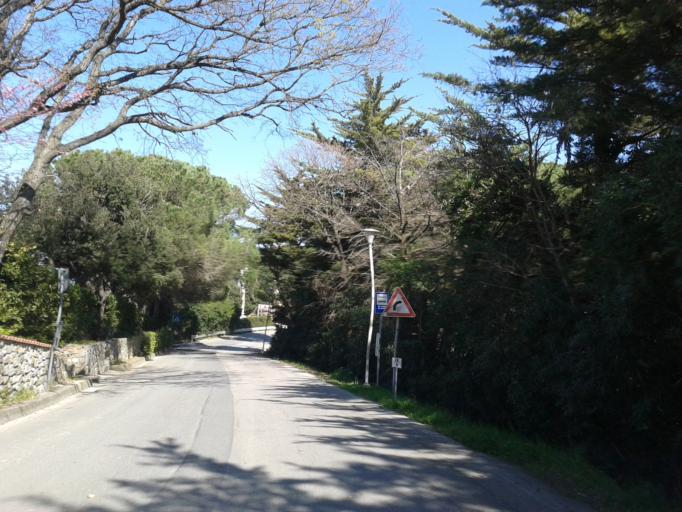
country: IT
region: Tuscany
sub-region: Provincia di Livorno
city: Quercianella
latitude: 43.4632
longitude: 10.4201
